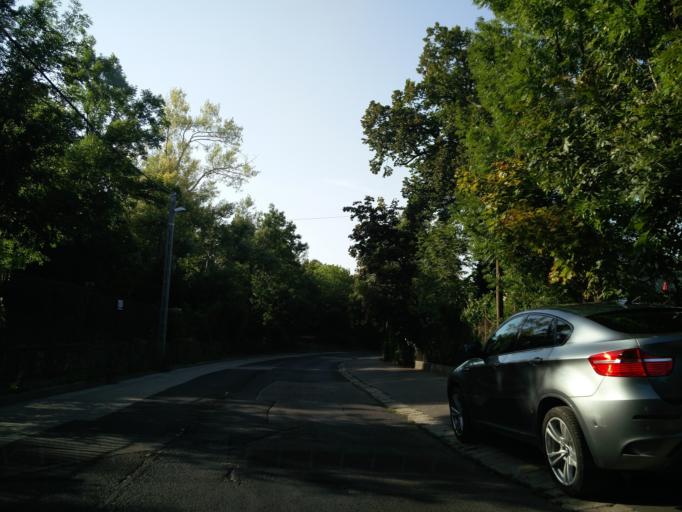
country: HU
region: Budapest
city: Budapest XII. keruelet
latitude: 47.5045
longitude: 18.9829
